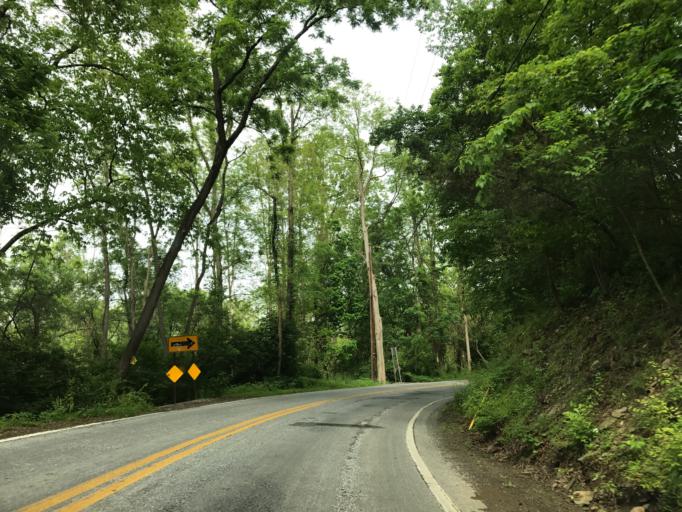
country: US
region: Pennsylvania
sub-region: York County
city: Susquehanna Trails
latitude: 39.7804
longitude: -76.4151
